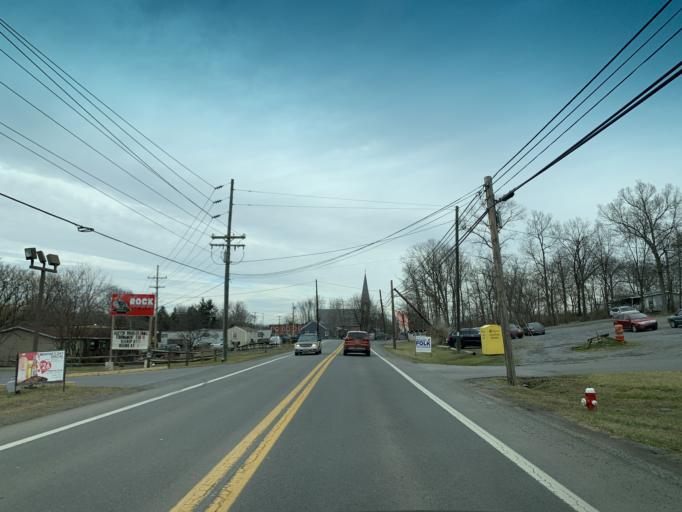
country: US
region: West Virginia
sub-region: Berkeley County
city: Martinsburg
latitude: 39.5072
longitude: -77.9352
